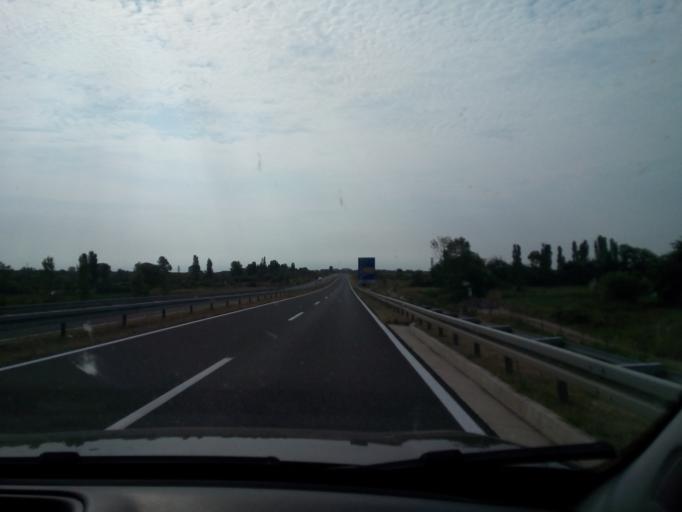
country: HR
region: Zadarska
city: Bibinje
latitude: 44.0945
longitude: 15.3004
